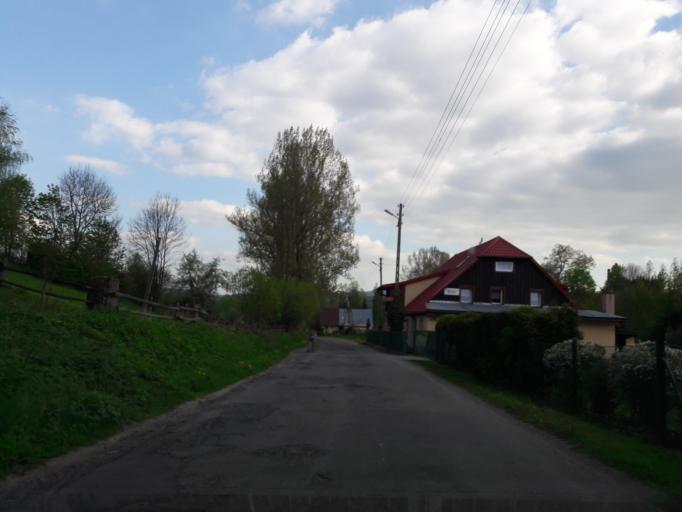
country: PL
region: Lower Silesian Voivodeship
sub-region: Powiat klodzki
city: Duszniki-Zdroj
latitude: 50.4317
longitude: 16.3588
